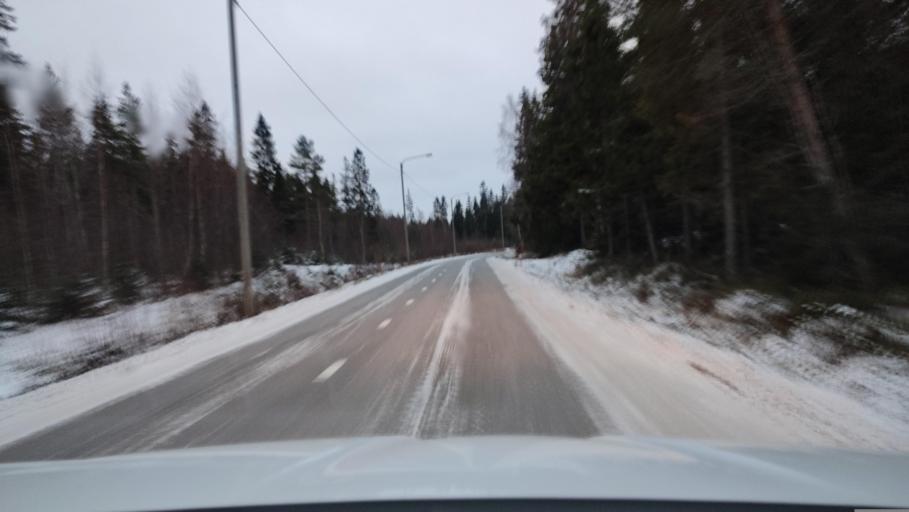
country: FI
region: Ostrobothnia
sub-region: Vaasa
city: Replot
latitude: 63.3572
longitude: 21.3034
